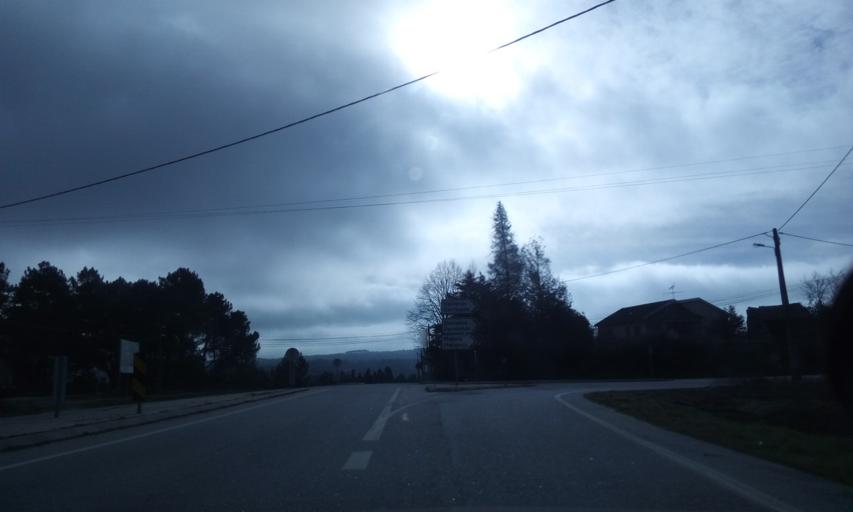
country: PT
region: Guarda
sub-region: Aguiar da Beira
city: Aguiar da Beira
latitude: 40.7898
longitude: -7.5066
